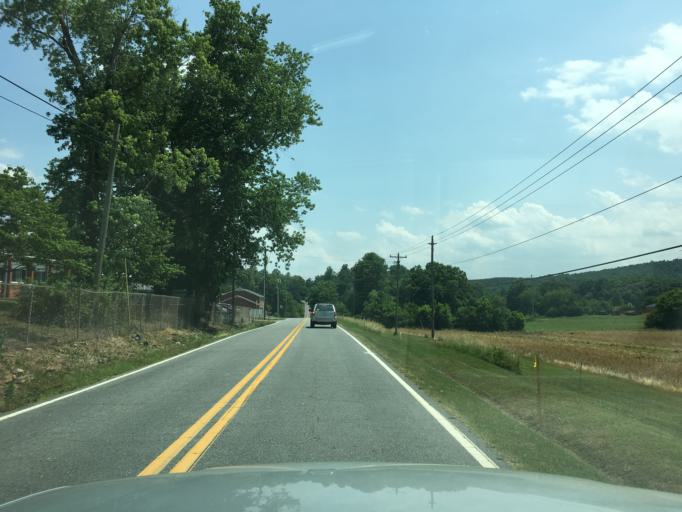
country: US
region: North Carolina
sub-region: McDowell County
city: West Marion
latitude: 35.6135
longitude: -81.9820
